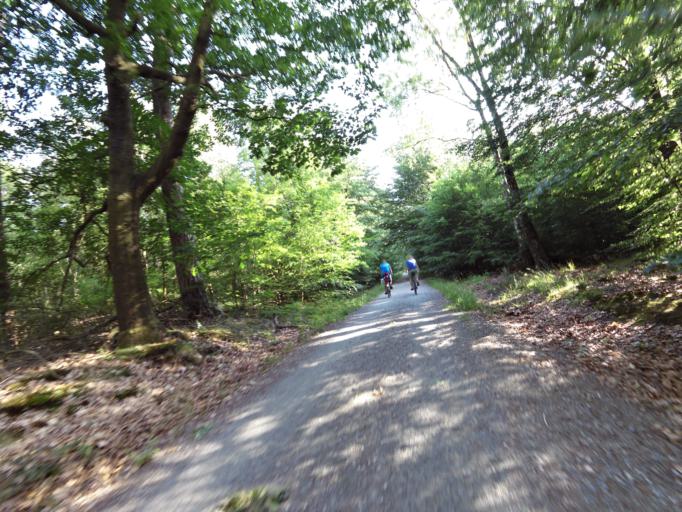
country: DE
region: Lower Saxony
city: Nordholz
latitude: 53.8540
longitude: 8.6001
